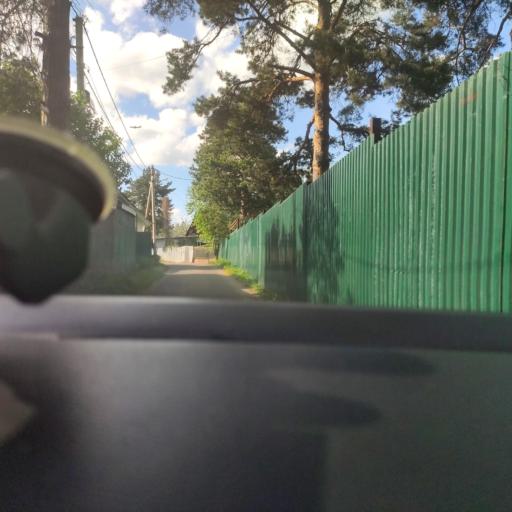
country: RU
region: Moskovskaya
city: Sheremet'yevskiy
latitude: 55.9953
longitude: 37.5451
